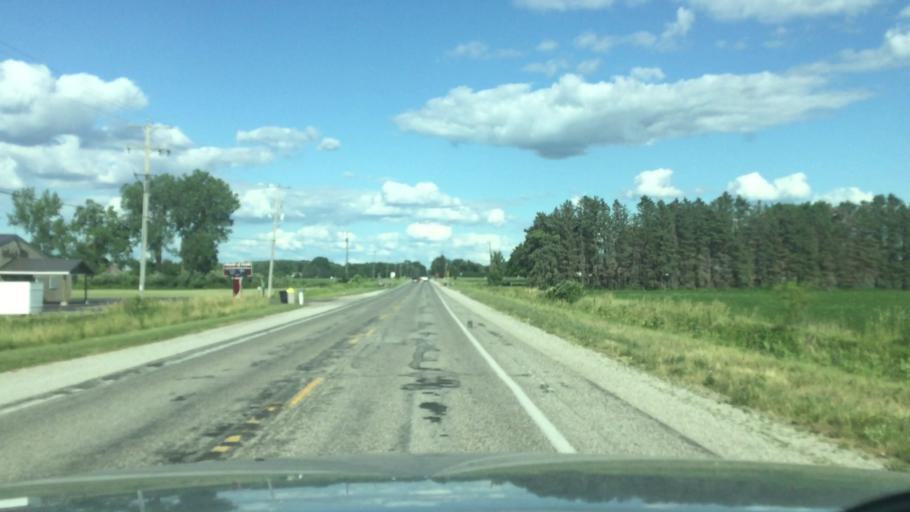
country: US
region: Michigan
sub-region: Saginaw County
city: Shields
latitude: 43.3798
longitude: -84.1185
